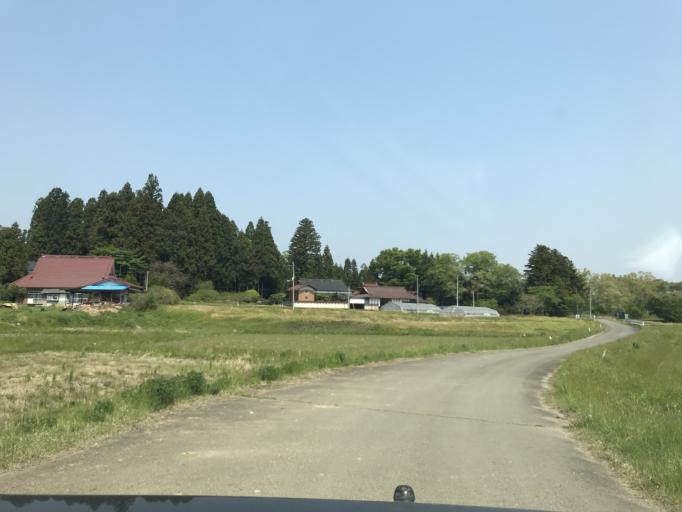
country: JP
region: Iwate
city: Ichinoseki
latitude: 38.8567
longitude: 141.0653
